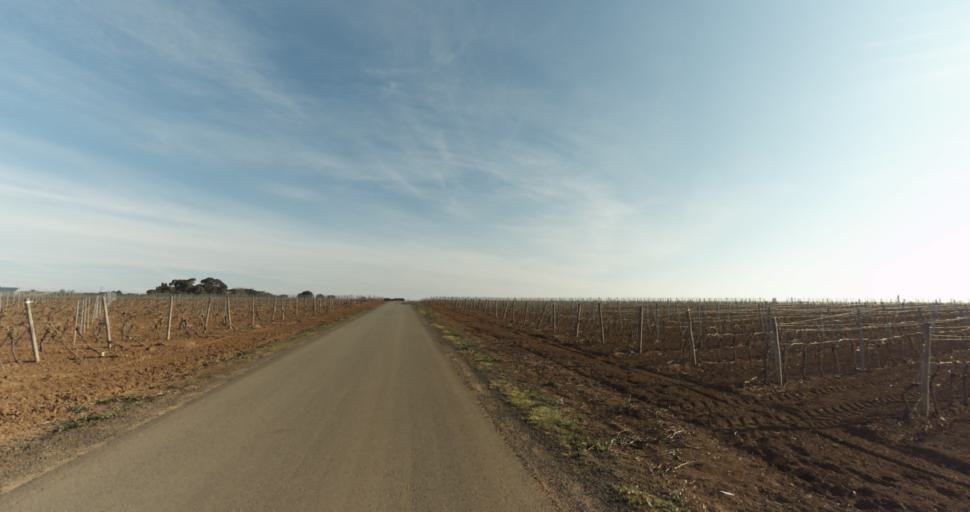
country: FR
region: Languedoc-Roussillon
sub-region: Departement de l'Herault
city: Marseillan
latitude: 43.3762
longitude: 3.5178
